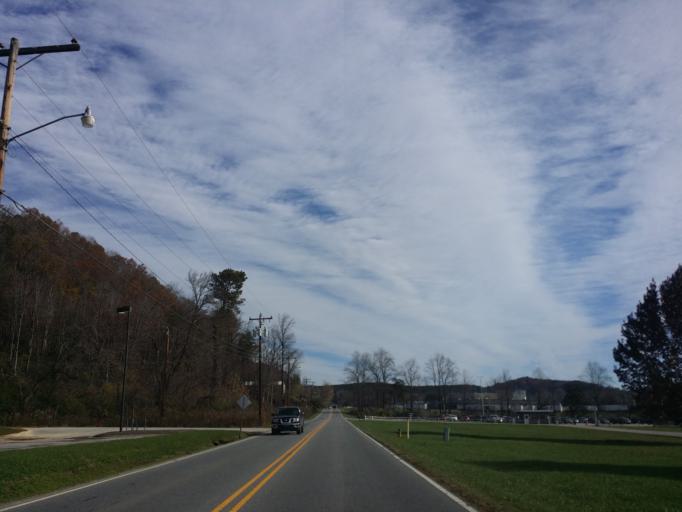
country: US
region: North Carolina
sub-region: McDowell County
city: West Marion
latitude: 35.6377
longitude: -82.1702
